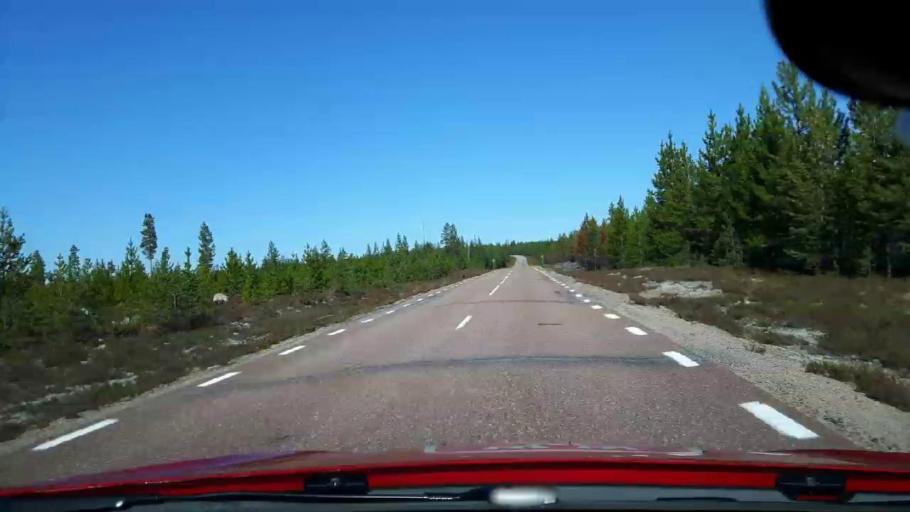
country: SE
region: Jaemtland
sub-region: Harjedalens Kommun
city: Sveg
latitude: 61.7136
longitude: 14.1688
